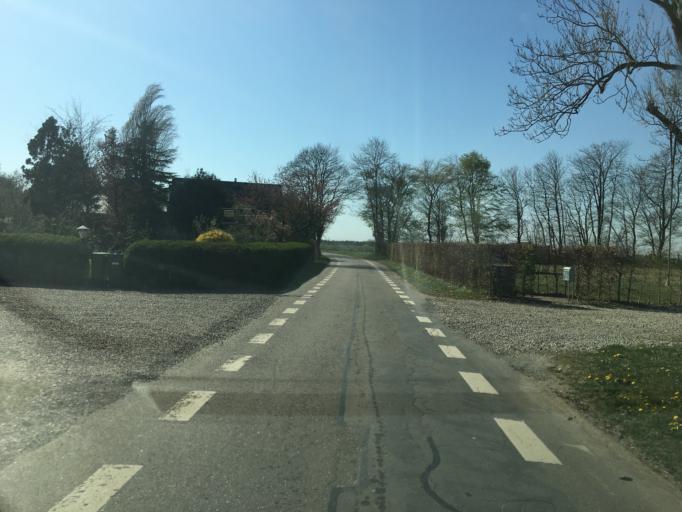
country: DK
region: South Denmark
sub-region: Aabenraa Kommune
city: Rodekro
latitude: 55.0708
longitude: 9.2936
